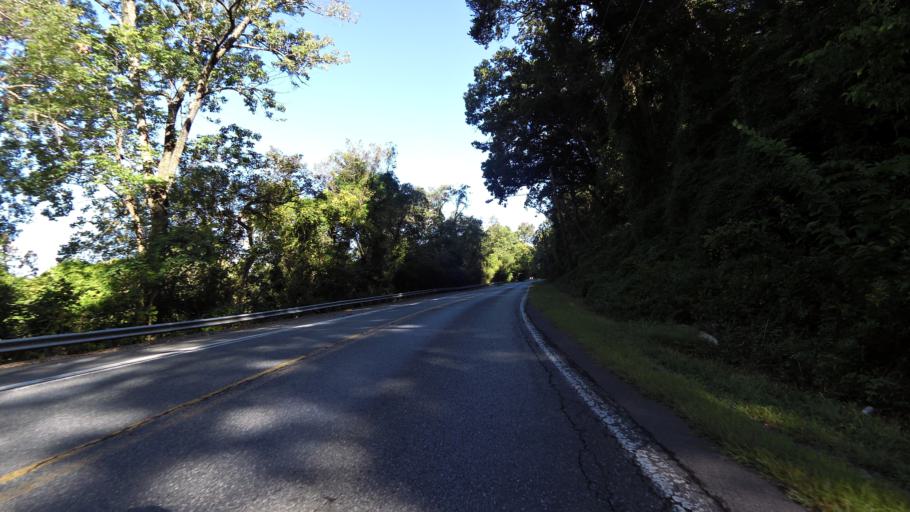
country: US
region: Maryland
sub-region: Montgomery County
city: Brookmont
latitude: 38.9514
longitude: -77.1269
